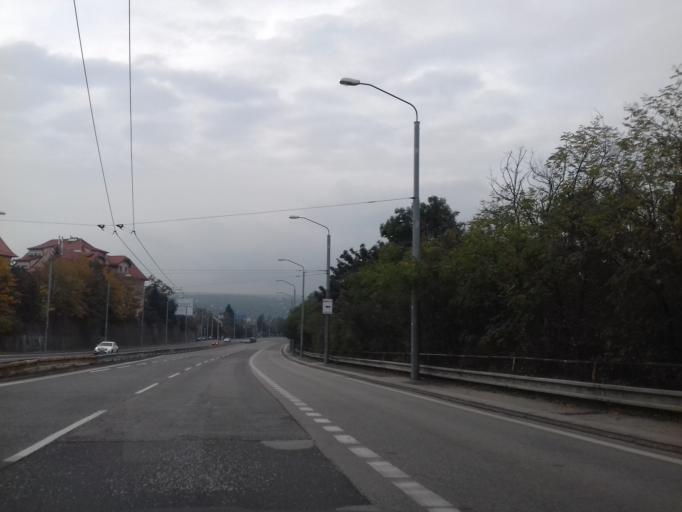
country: SK
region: Bratislavsky
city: Bratislava
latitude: 48.1633
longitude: 17.0912
